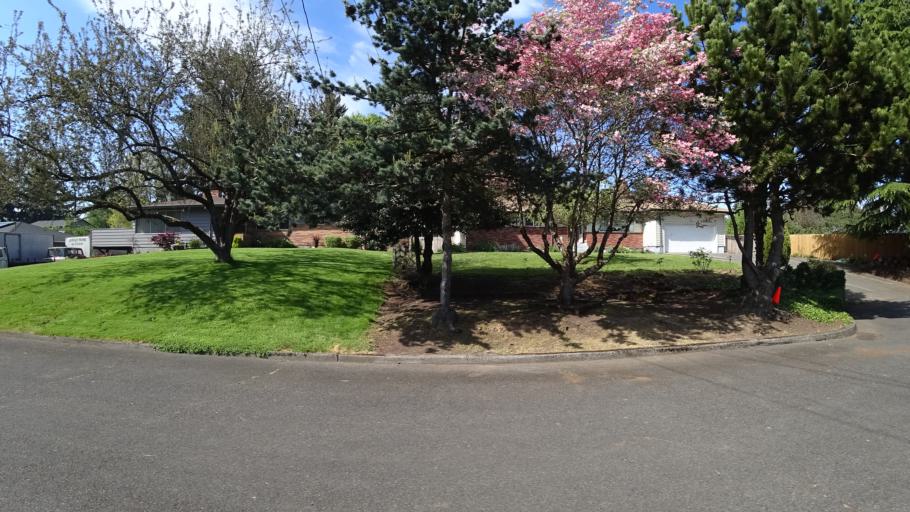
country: US
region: Oregon
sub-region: Clackamas County
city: Milwaukie
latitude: 45.4596
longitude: -122.6229
